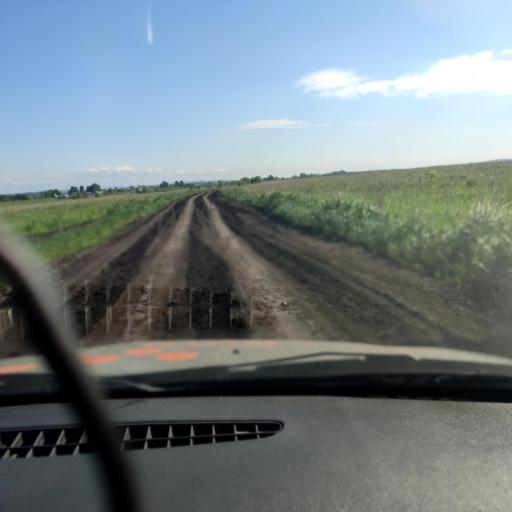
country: RU
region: Bashkortostan
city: Avdon
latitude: 54.5675
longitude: 55.8324
